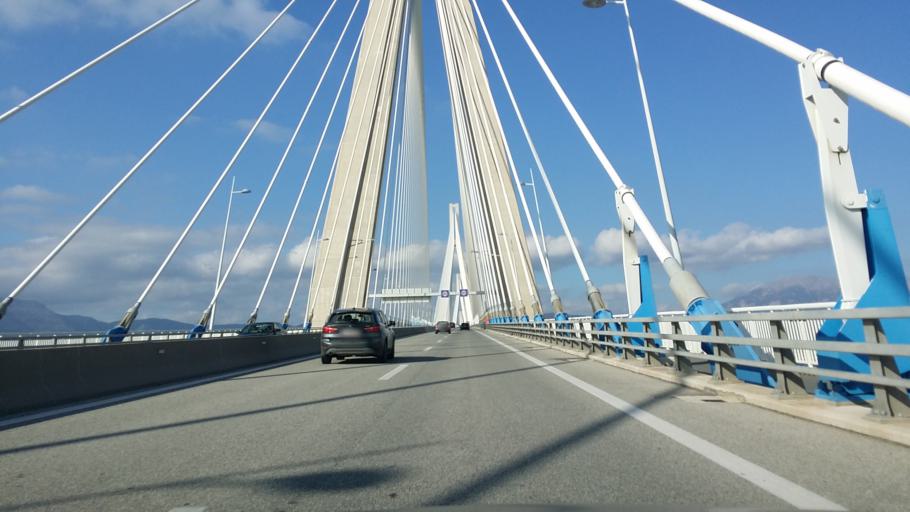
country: GR
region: West Greece
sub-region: Nomos Achaias
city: Rio
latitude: 38.3123
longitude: 21.7778
